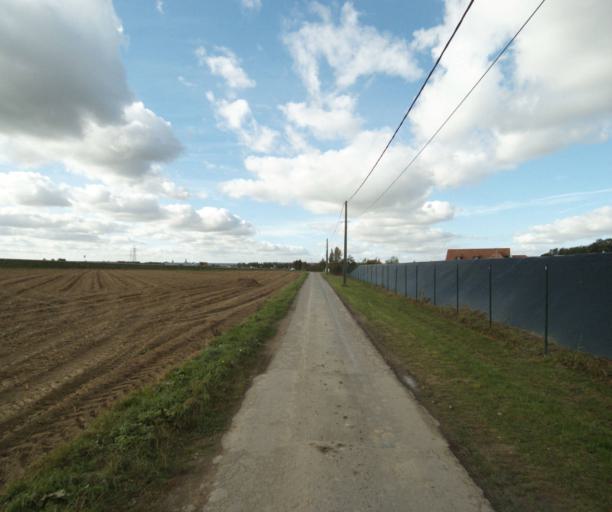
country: FR
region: Nord-Pas-de-Calais
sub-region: Departement du Nord
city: Houplines
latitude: 50.6763
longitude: 2.9222
